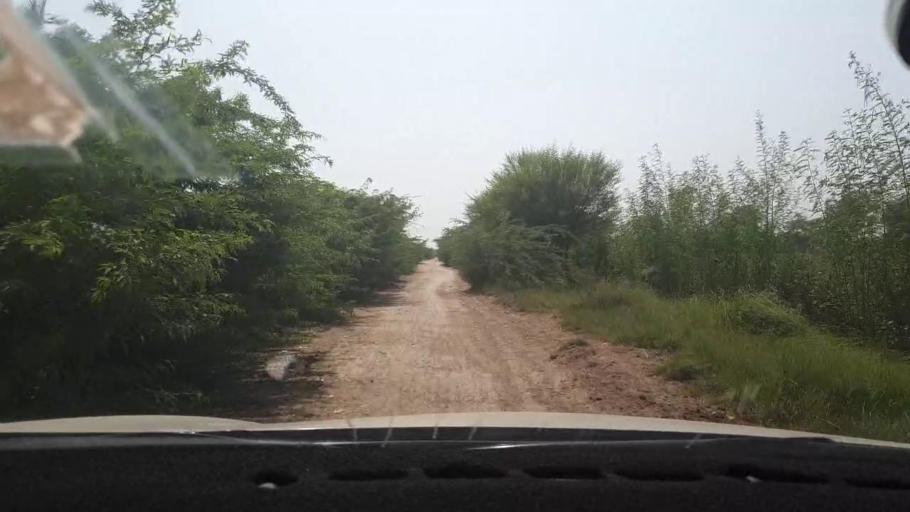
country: PK
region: Sindh
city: Tando Mittha Khan
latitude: 25.9268
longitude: 69.2247
